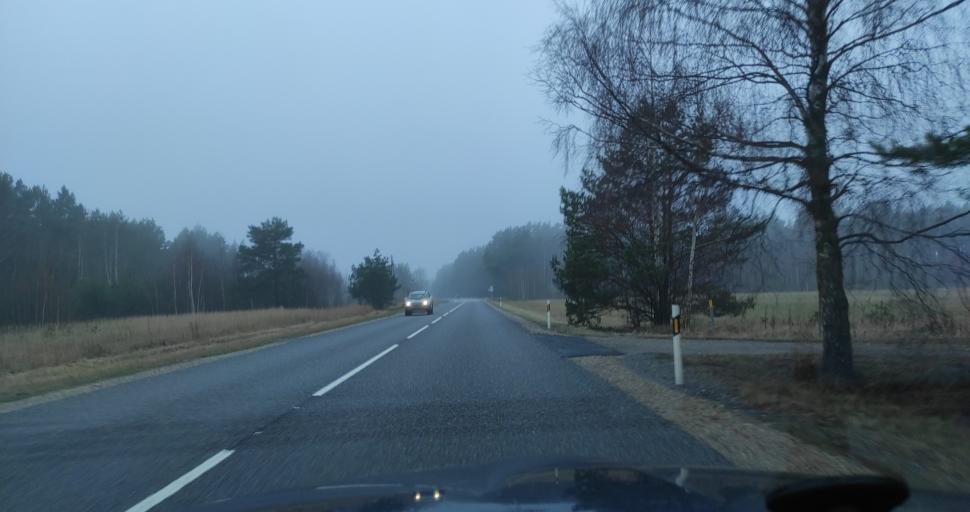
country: LV
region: Pavilostas
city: Pavilosta
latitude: 56.9503
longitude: 21.3052
